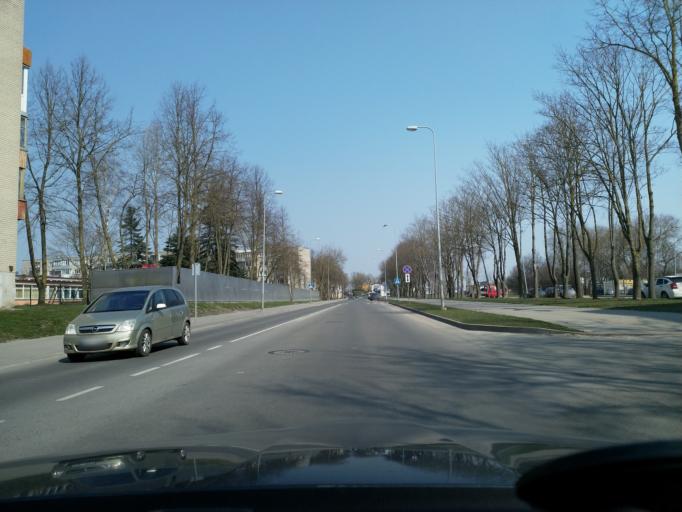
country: LT
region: Klaipedos apskritis
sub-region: Klaipeda
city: Klaipeda
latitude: 55.6982
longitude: 21.1626
